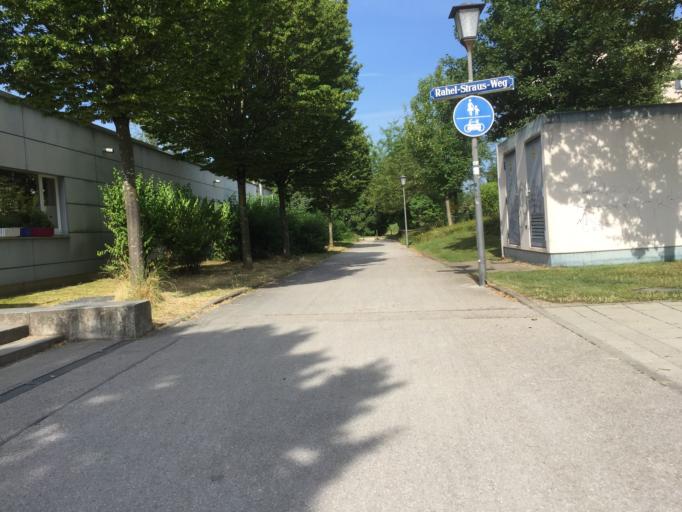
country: DE
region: Bavaria
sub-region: Upper Bavaria
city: Bogenhausen
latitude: 48.1234
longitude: 11.6355
